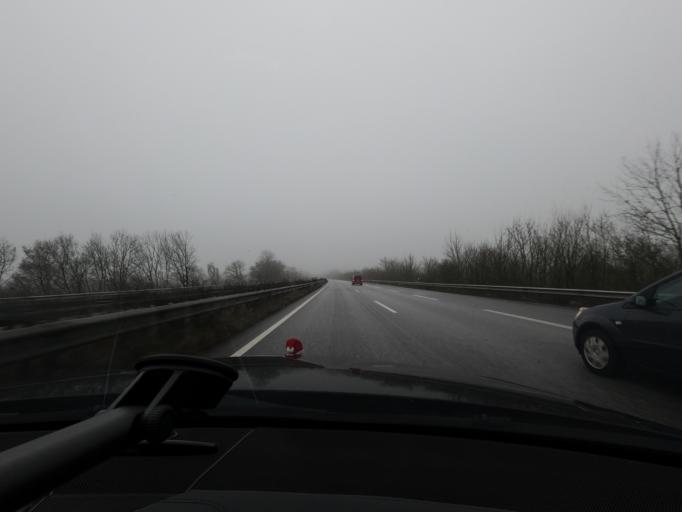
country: DE
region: Schleswig-Holstein
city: Dannewerk
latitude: 54.5028
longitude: 9.5073
